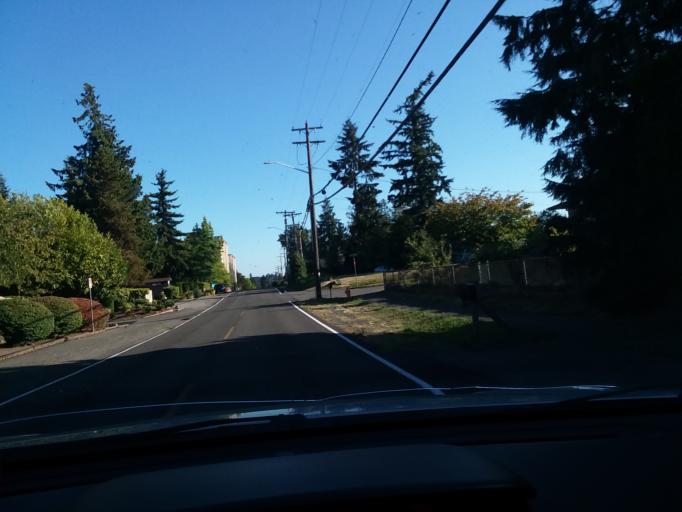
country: US
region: Washington
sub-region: Snohomish County
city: Alderwood Manor
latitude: 47.8242
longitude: -122.2871
